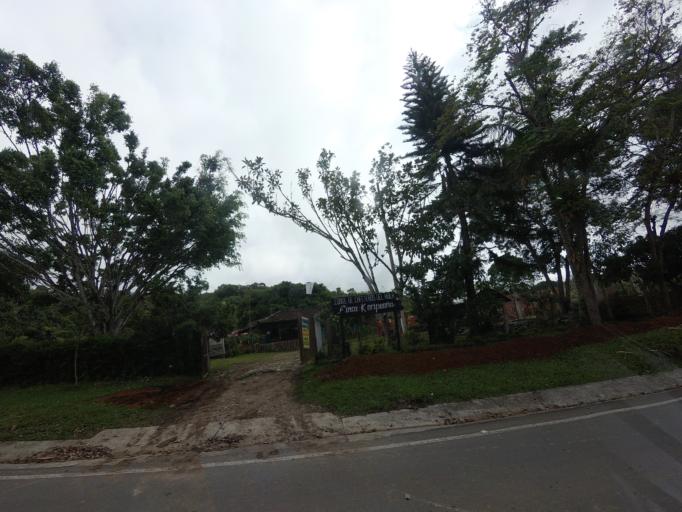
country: CO
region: Huila
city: San Agustin
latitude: 1.8878
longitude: -76.2848
